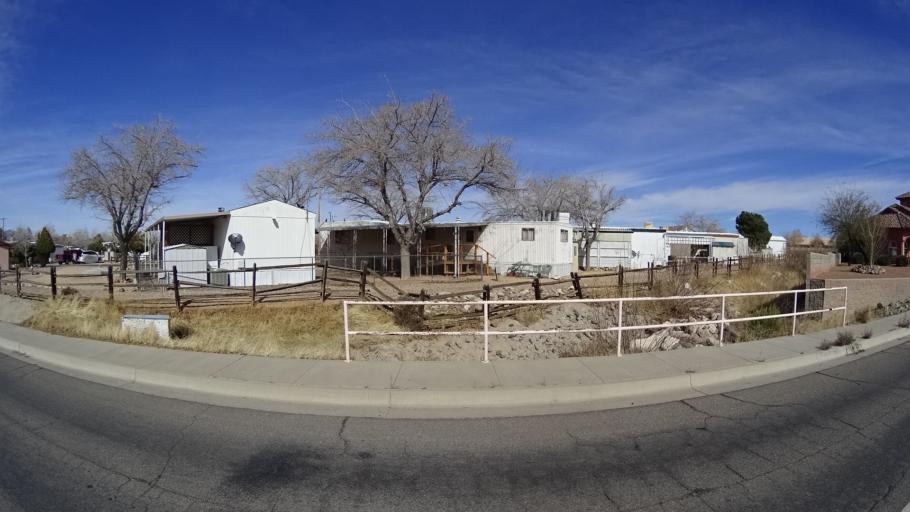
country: US
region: Arizona
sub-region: Mohave County
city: Kingman
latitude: 35.1885
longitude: -114.0108
